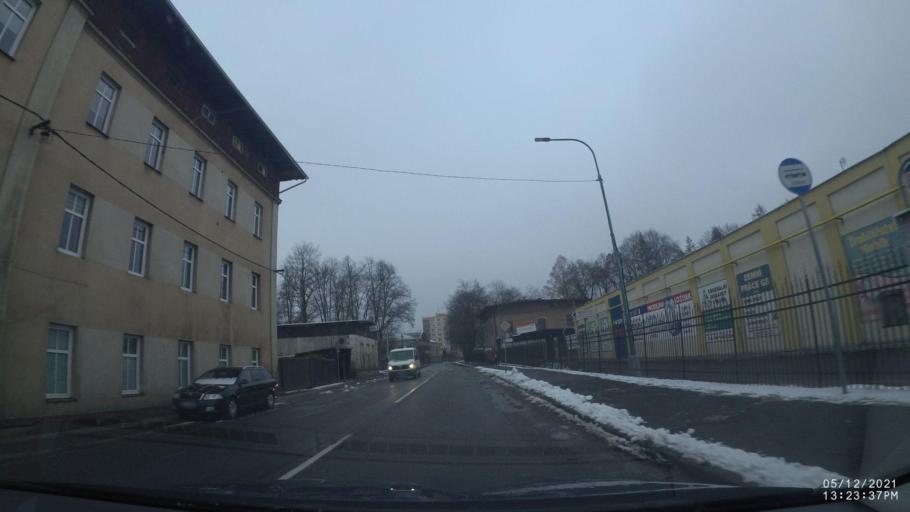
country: CZ
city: Hronov
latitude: 50.4729
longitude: 16.1795
